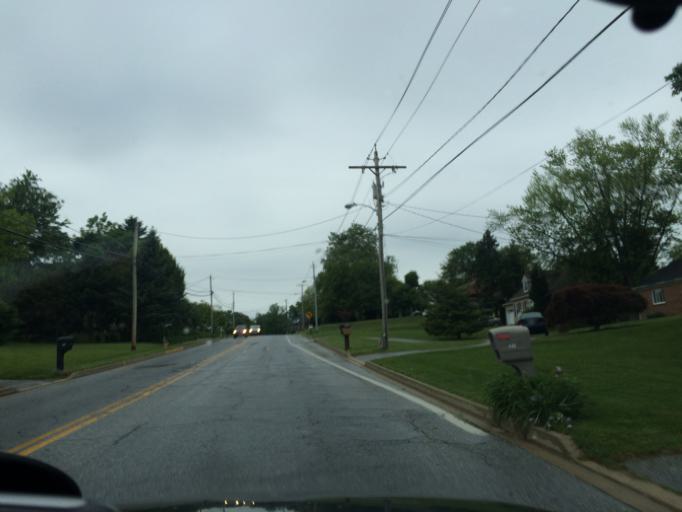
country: US
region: Maryland
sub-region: Carroll County
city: Westminster
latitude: 39.5829
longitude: -77.0127
